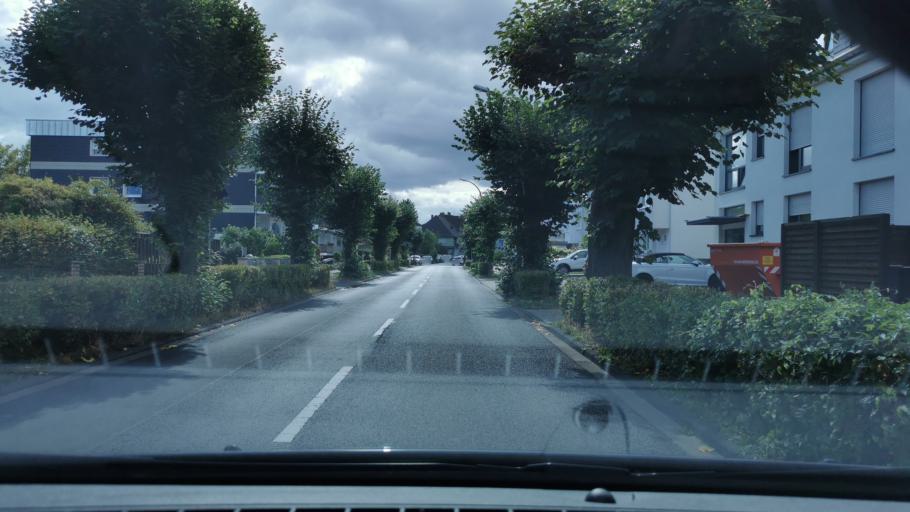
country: DE
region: North Rhine-Westphalia
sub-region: Regierungsbezirk Koln
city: Porz am Rhein
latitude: 50.8764
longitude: 7.0287
